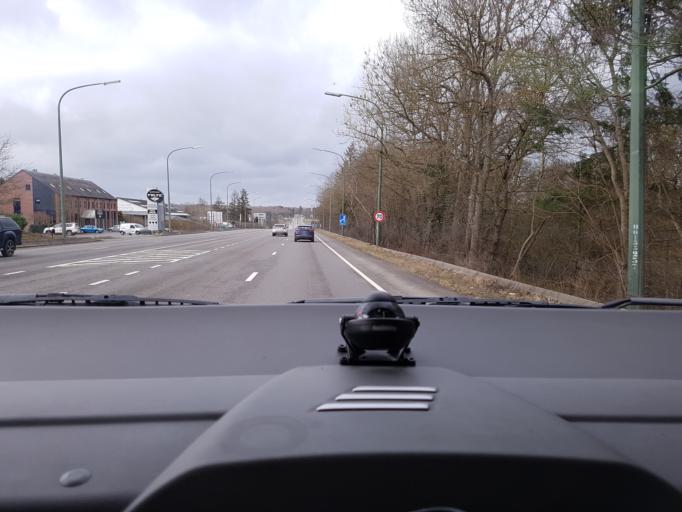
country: BE
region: Wallonia
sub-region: Province du Luxembourg
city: Marche-en-Famenne
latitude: 50.2311
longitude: 5.3235
